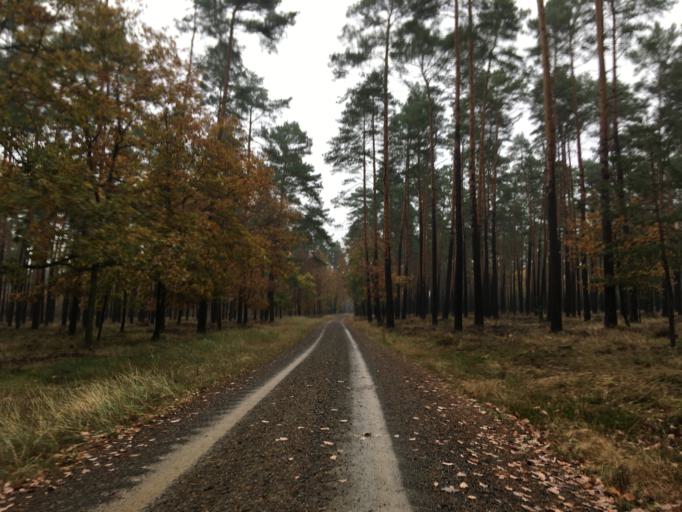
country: DE
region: Brandenburg
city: Beeskow
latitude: 52.2368
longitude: 14.2876
